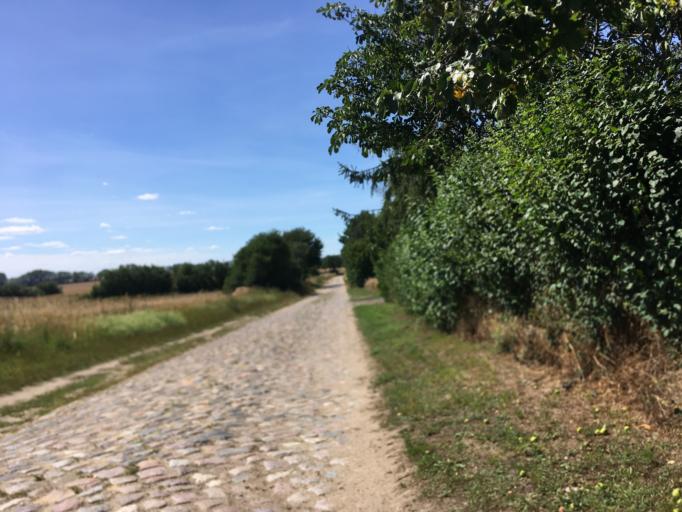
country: DE
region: Brandenburg
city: Brussow
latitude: 53.3234
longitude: 14.0991
